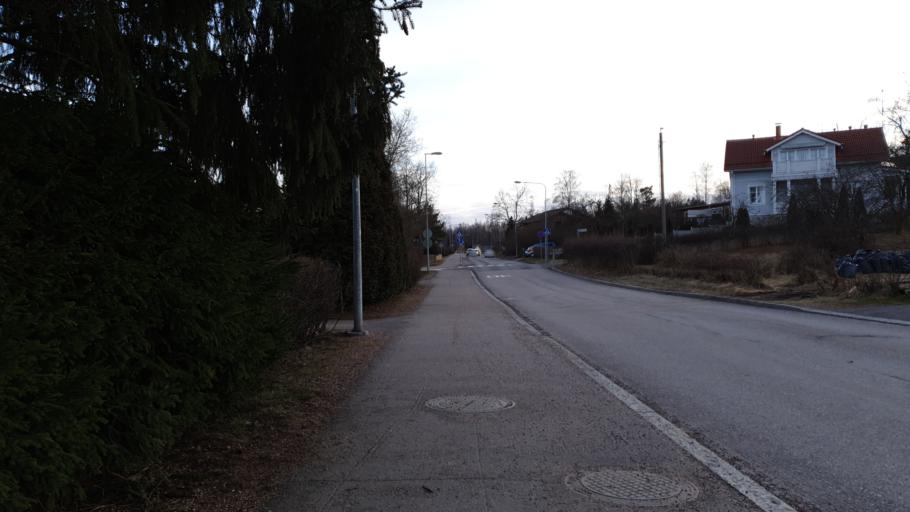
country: FI
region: Uusimaa
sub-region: Helsinki
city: Vantaa
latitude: 60.3117
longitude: 25.0079
